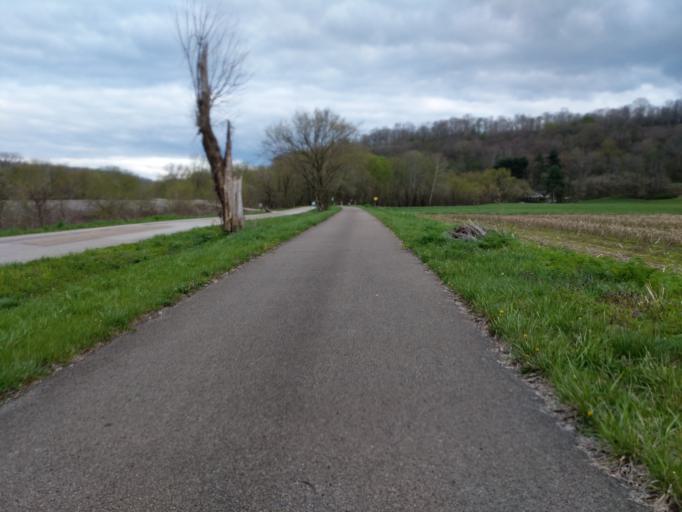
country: US
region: Ohio
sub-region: Athens County
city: Chauncey
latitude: 39.3891
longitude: -82.1272
